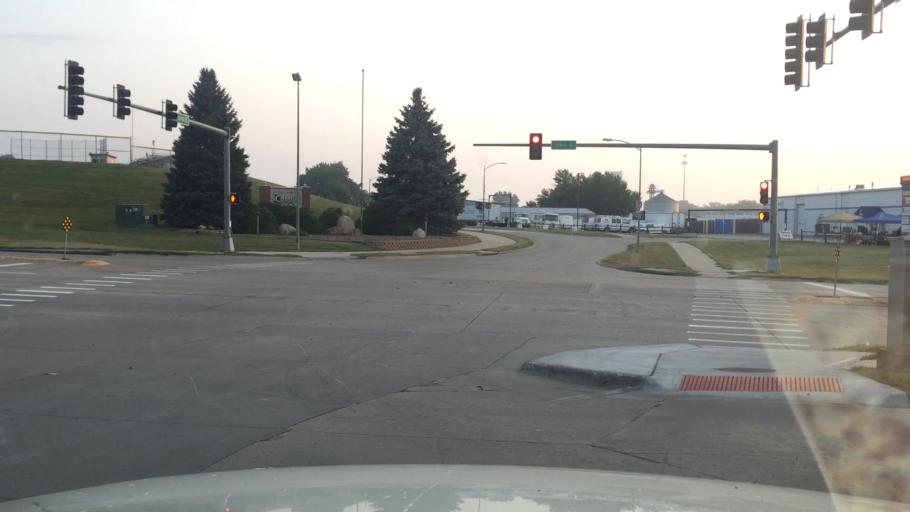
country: US
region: Iowa
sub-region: Warren County
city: Carlisle
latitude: 41.4942
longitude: -93.4874
